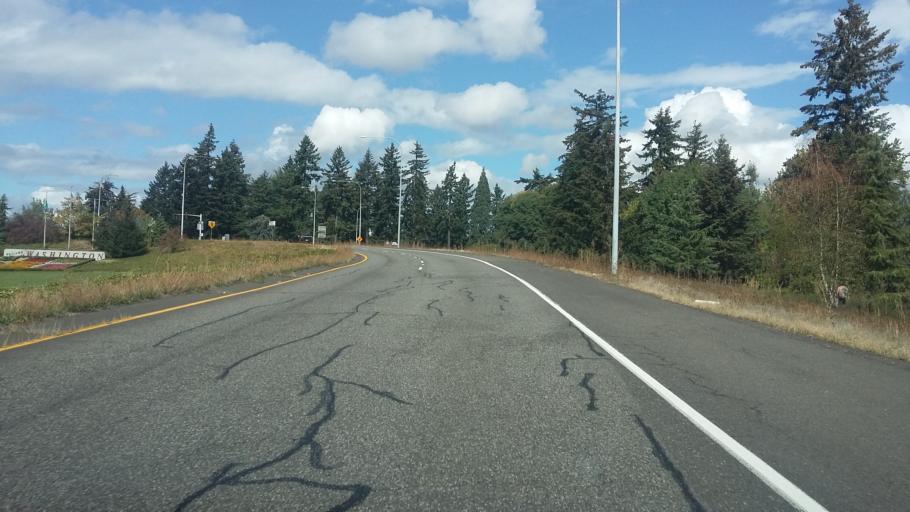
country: US
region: Washington
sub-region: Clark County
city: Vancouver
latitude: 45.6369
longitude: -122.6612
